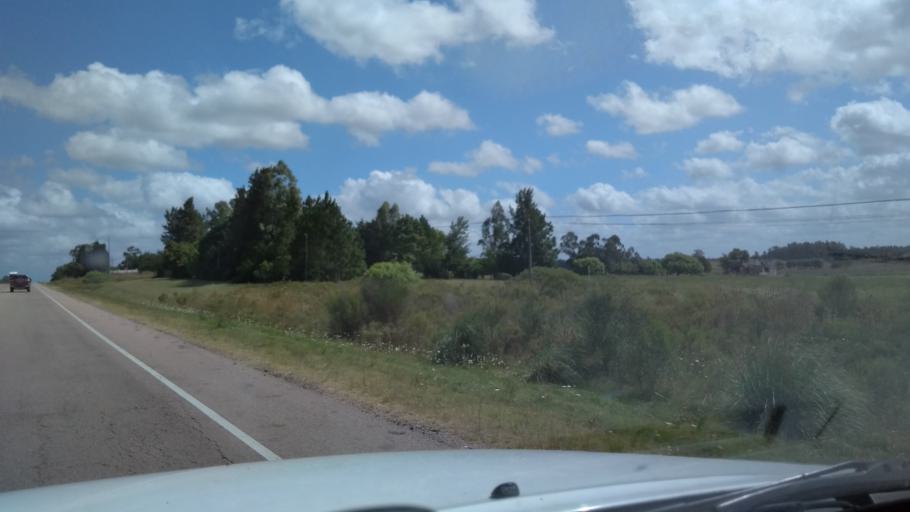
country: UY
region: Canelones
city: Sauce
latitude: -34.6220
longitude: -56.0502
